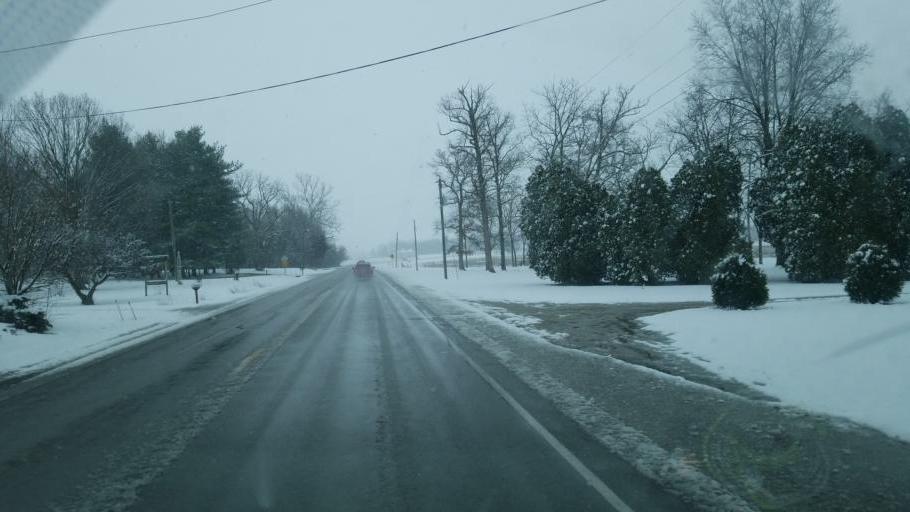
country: US
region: Indiana
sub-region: Randolph County
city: Parker City
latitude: 40.0851
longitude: -85.2784
